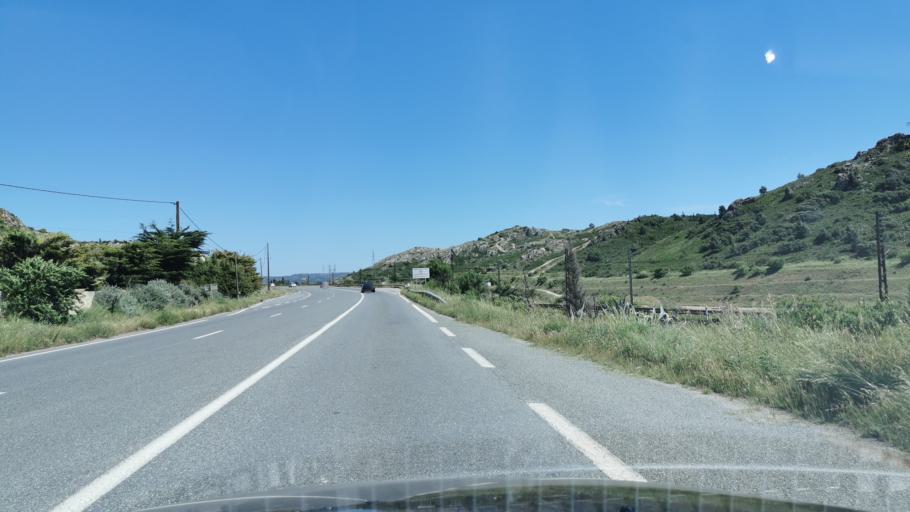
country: FR
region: Languedoc-Roussillon
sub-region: Departement de l'Aude
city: Narbonne
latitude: 43.1812
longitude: 2.9555
